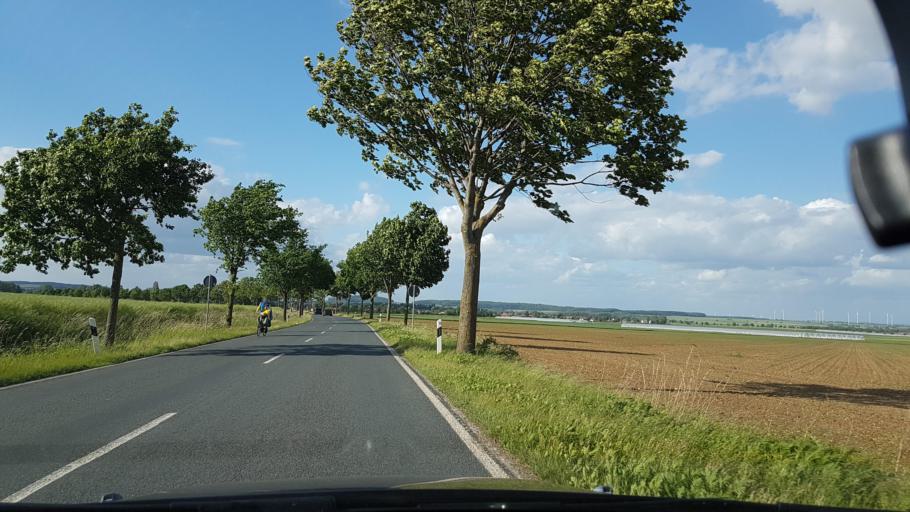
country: DE
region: Lower Saxony
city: Elze
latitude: 52.1458
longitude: 9.6669
